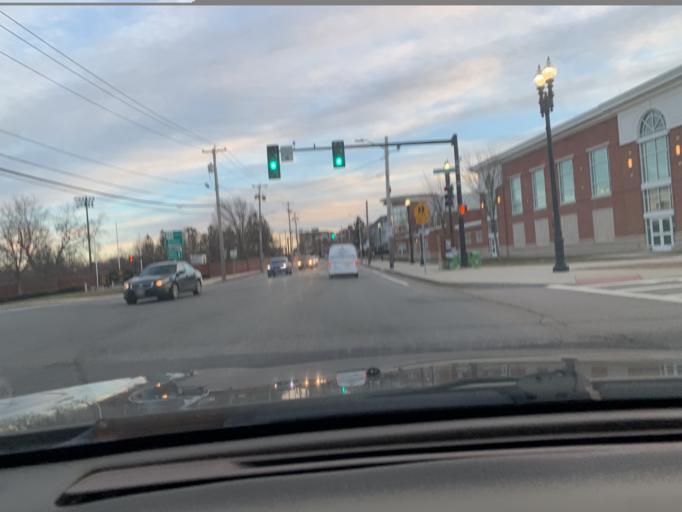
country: US
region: Massachusetts
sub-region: Norfolk County
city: Quincy
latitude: 42.2623
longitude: -71.0118
